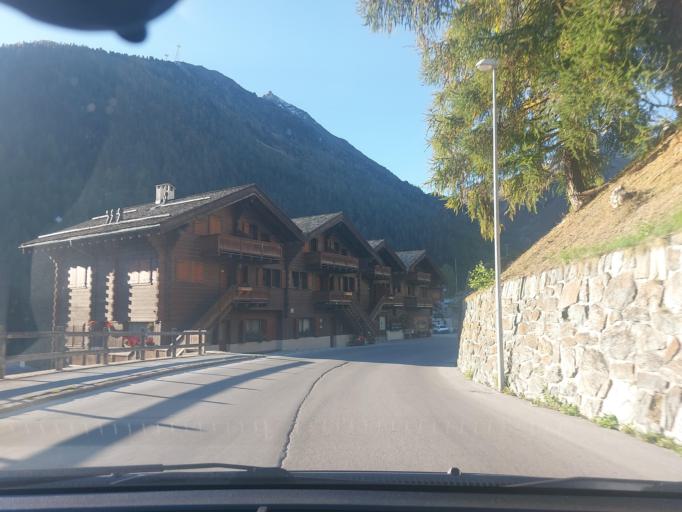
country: CH
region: Valais
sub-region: Herens District
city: Evolene
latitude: 46.1792
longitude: 7.5766
